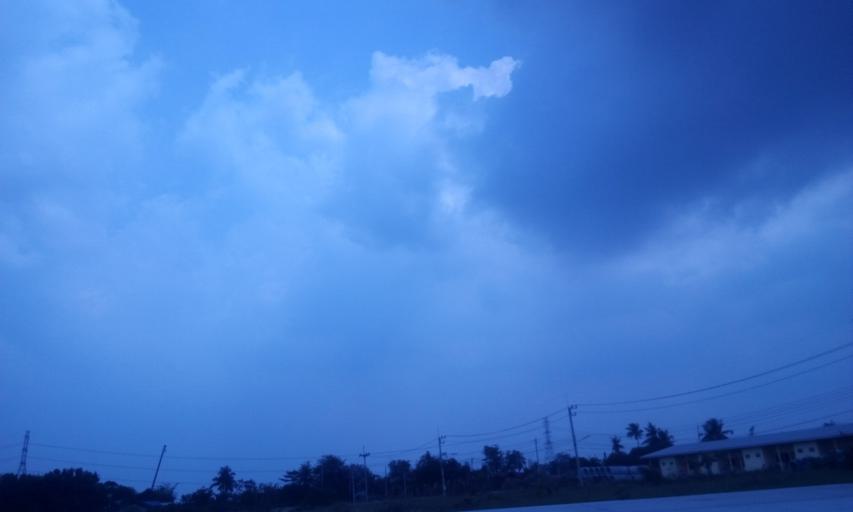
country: TH
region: Chon Buri
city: Ban Bueng
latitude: 13.3105
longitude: 101.1835
